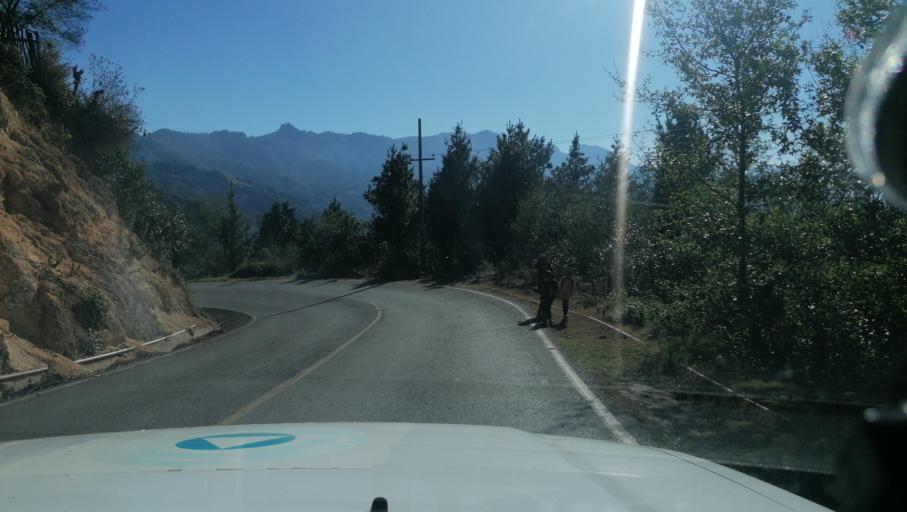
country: MX
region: Chiapas
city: Motozintla de Mendoza
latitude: 15.2516
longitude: -92.2217
